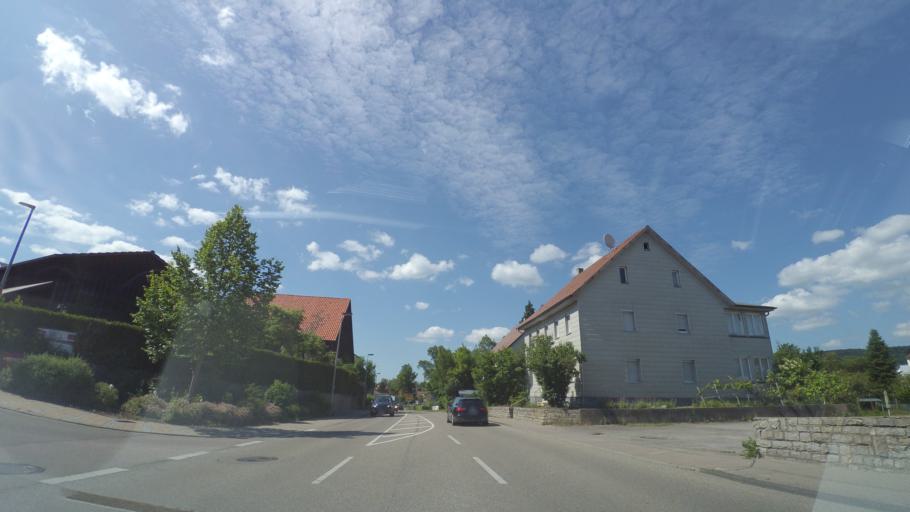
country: DE
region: Baden-Wuerttemberg
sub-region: Regierungsbezirk Stuttgart
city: Gaildorf
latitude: 48.9973
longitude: 9.7738
